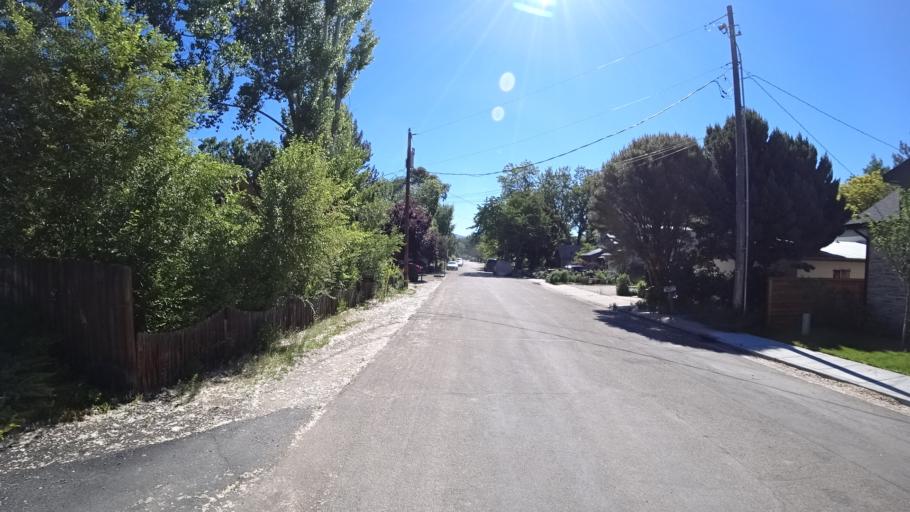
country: US
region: Idaho
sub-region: Ada County
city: Garden City
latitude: 43.6469
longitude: -116.2273
